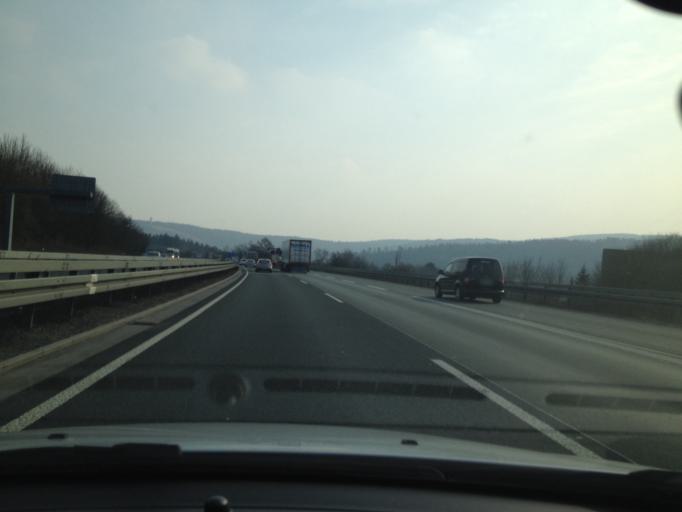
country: DE
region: Hesse
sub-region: Regierungsbezirk Giessen
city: Merkenbach
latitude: 50.6731
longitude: 8.2842
